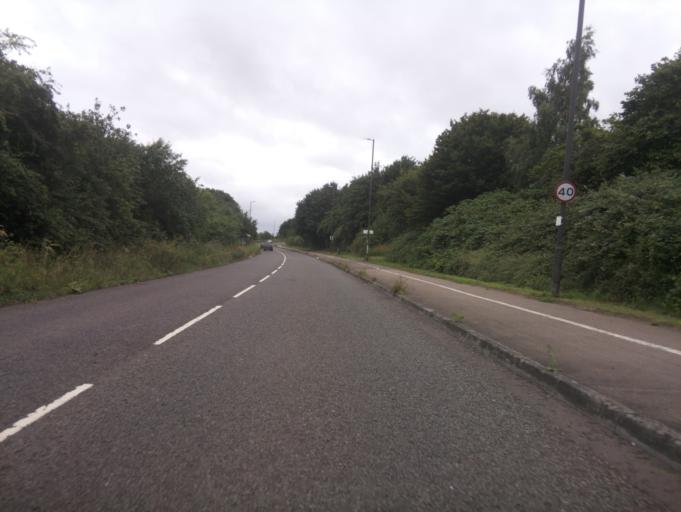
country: GB
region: England
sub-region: Gloucestershire
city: Tewkesbury
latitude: 51.9784
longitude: -2.1507
